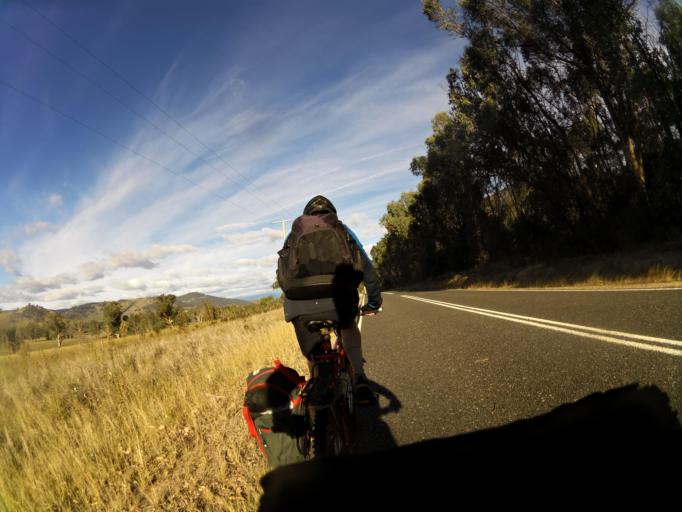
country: AU
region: New South Wales
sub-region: Greater Hume Shire
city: Holbrook
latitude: -35.9855
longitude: 147.8273
